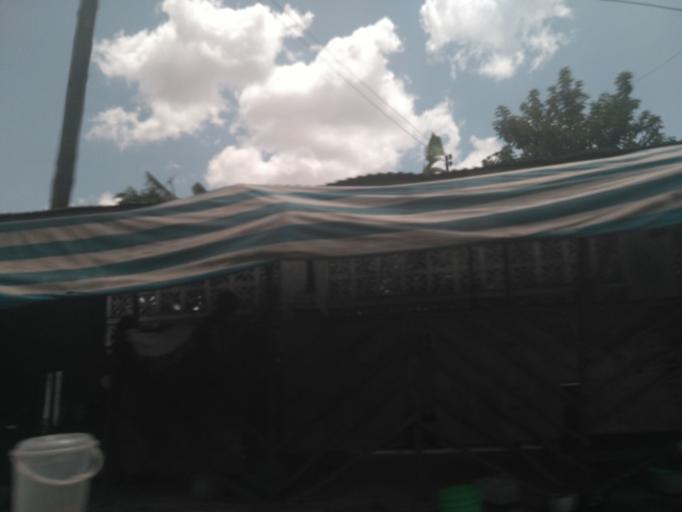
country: TZ
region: Dar es Salaam
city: Dar es Salaam
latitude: -6.8483
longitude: 39.2644
